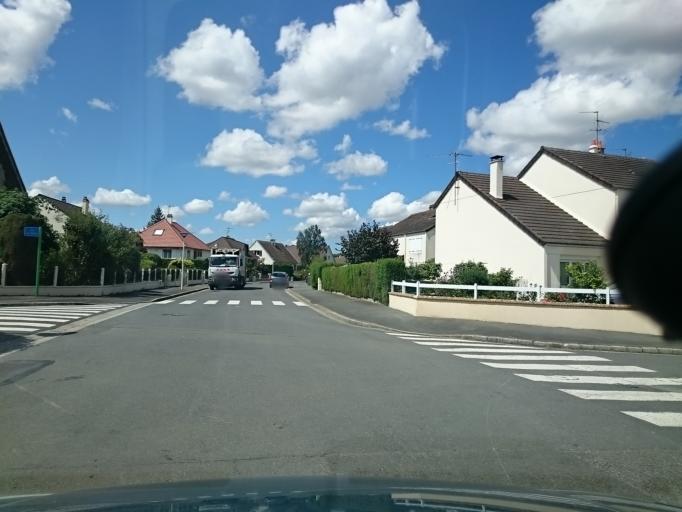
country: FR
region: Lower Normandy
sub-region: Departement du Calvados
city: Ifs
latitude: 49.1384
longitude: -0.3551
